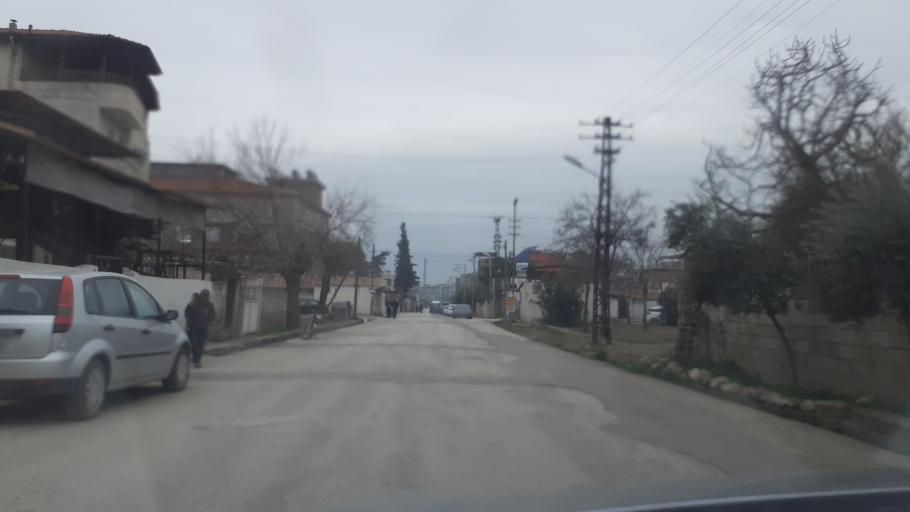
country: TR
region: Hatay
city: Kirikhan
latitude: 36.4887
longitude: 36.3557
